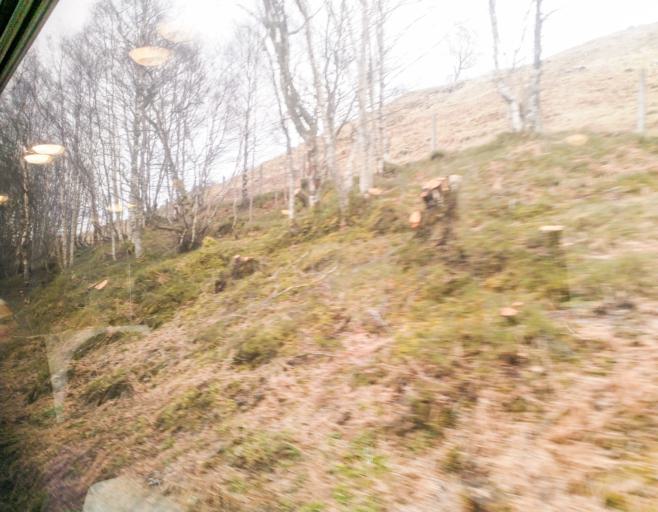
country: GB
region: Scotland
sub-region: Highland
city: Spean Bridge
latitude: 56.7884
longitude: -4.7290
